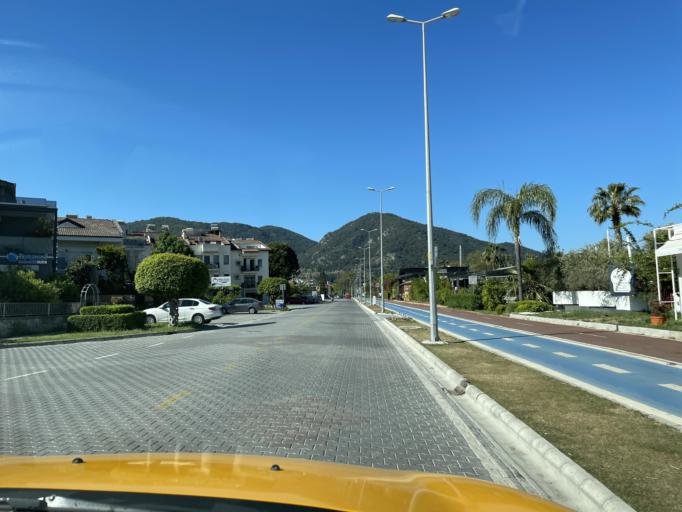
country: TR
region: Mugla
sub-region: Fethiye
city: Fethiye
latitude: 36.6333
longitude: 29.1201
